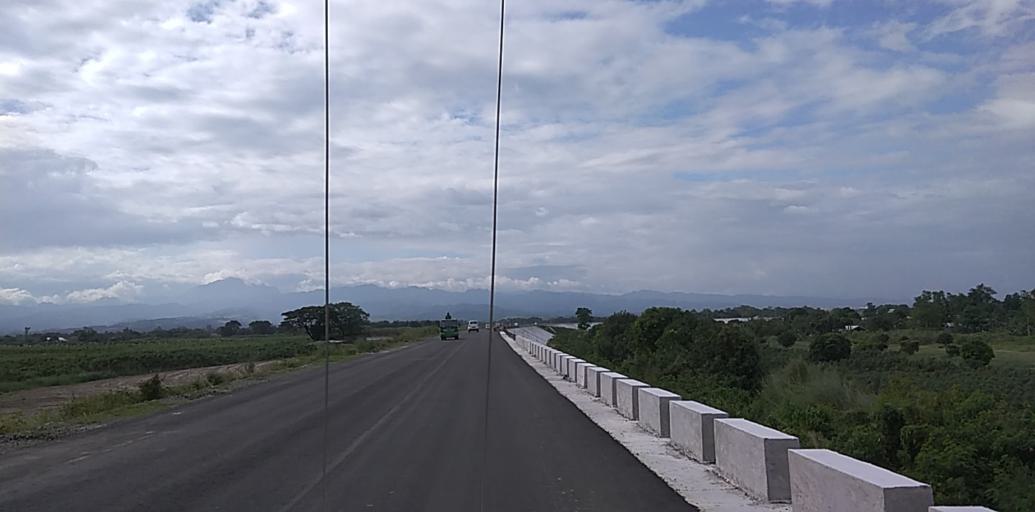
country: PH
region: Central Luzon
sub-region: Province of Pampanga
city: Pulung Santol
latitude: 15.0601
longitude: 120.5654
